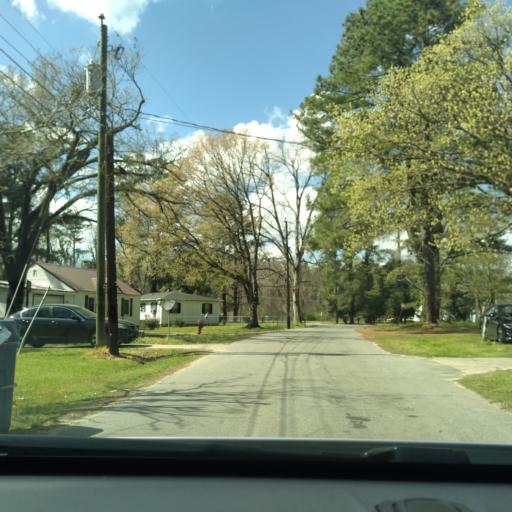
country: US
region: North Carolina
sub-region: Washington County
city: Plymouth
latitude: 35.8611
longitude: -76.7527
